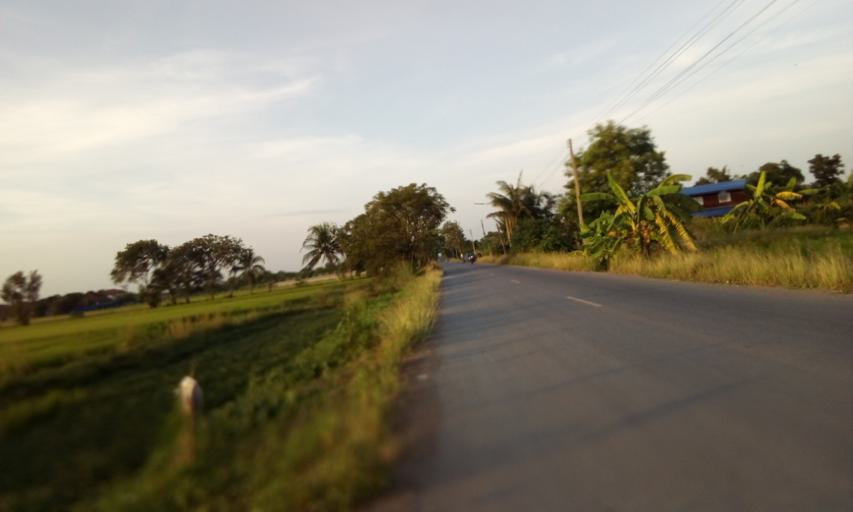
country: TH
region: Pathum Thani
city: Nong Suea
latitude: 14.0452
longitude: 100.8669
